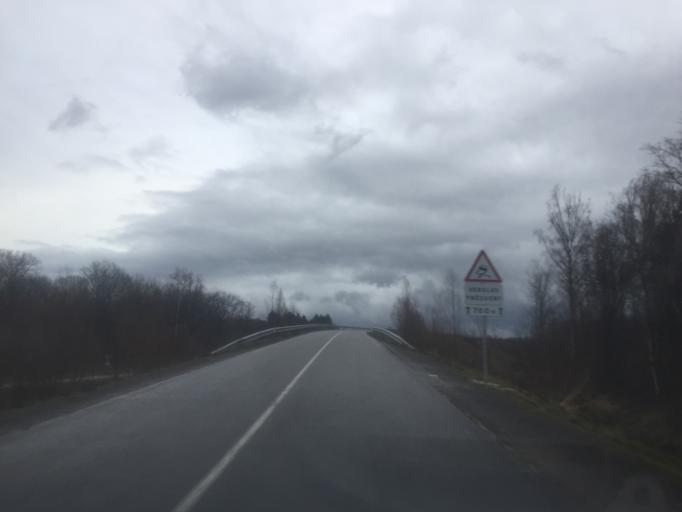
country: FR
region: Bourgogne
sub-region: Departement de la Cote-d'Or
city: Auxonne
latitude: 47.2283
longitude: 5.4783
